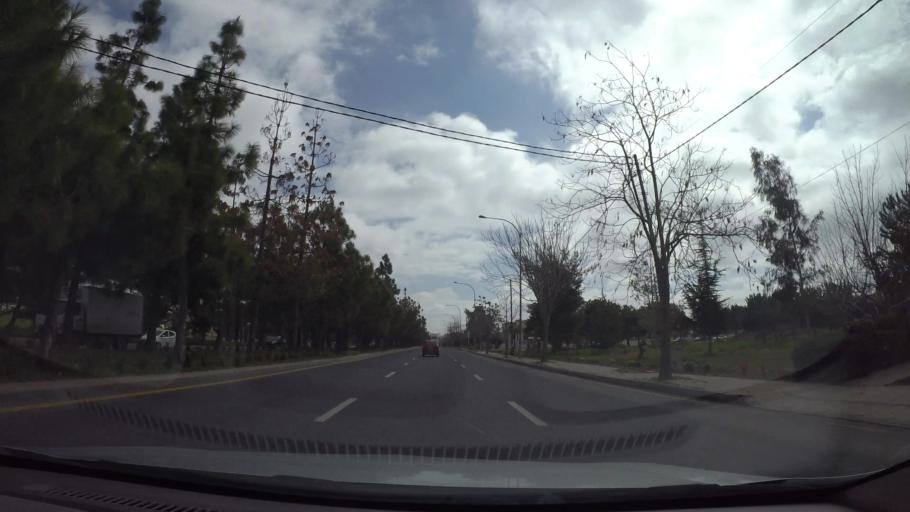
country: JO
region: Amman
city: Wadi as Sir
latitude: 31.9933
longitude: 35.8219
